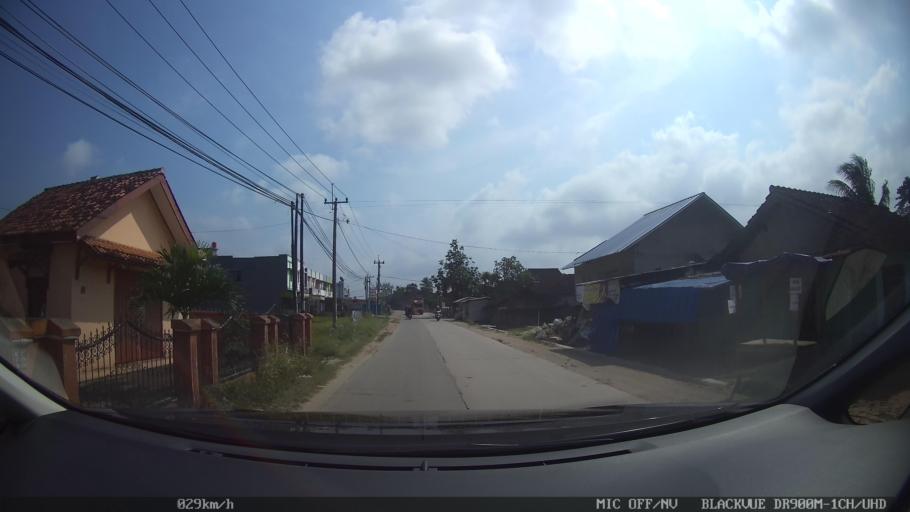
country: ID
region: Lampung
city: Kedaton
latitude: -5.3504
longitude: 105.2649
